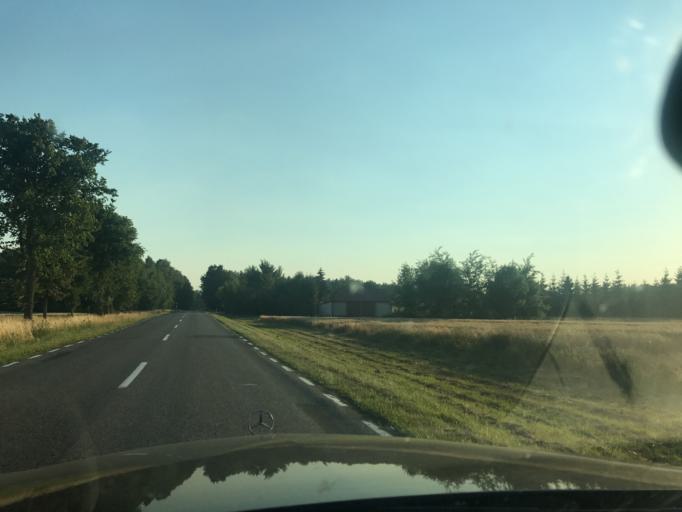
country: PL
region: Lublin Voivodeship
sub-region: Powiat parczewski
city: Jablon
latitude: 51.7070
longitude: 23.0687
